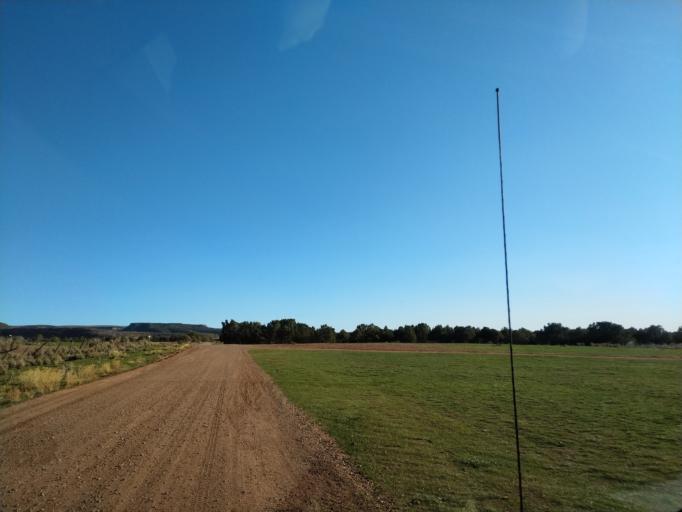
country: US
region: Colorado
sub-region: Mesa County
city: Loma
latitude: 38.9503
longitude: -109.0534
